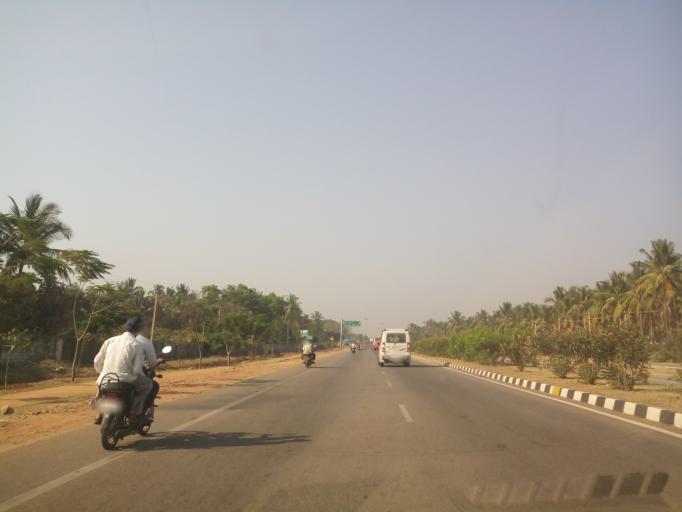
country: IN
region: Karnataka
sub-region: Bangalore Rural
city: Nelamangala
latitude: 13.0744
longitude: 77.3647
